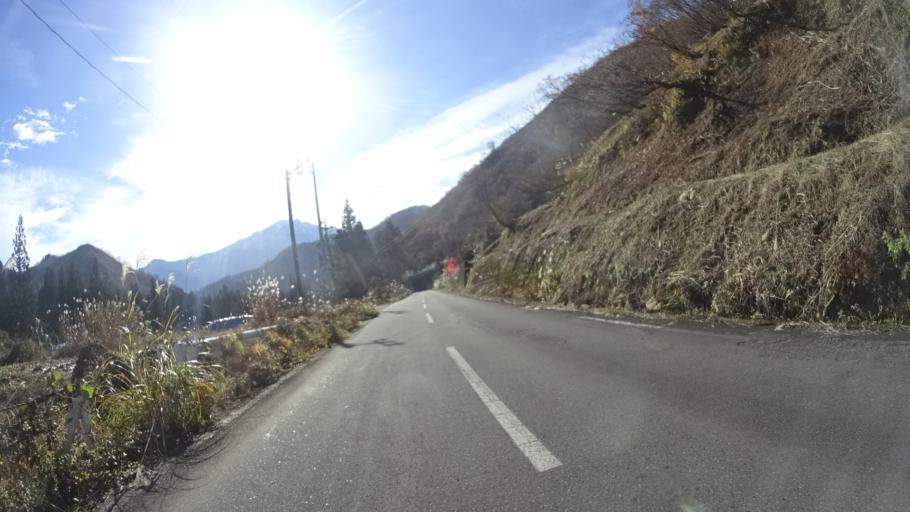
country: JP
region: Niigata
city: Muikamachi
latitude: 37.1886
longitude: 139.0820
